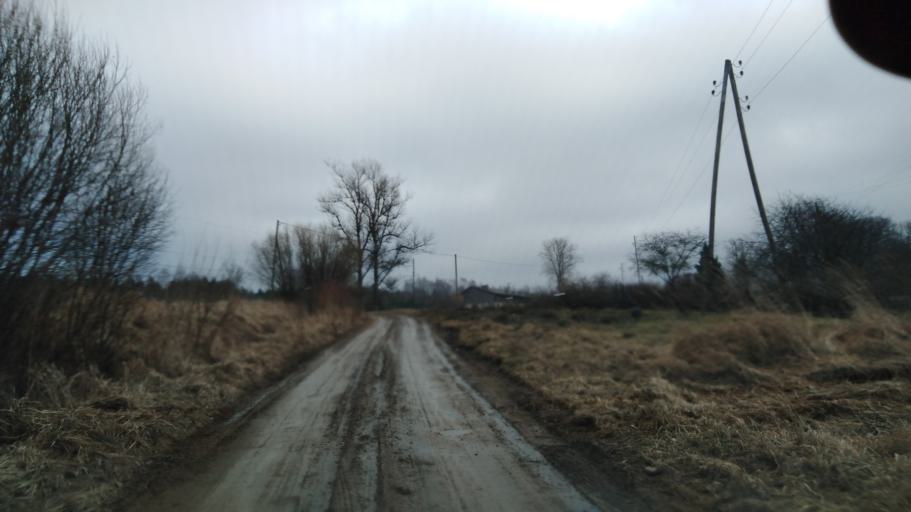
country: LV
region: Kuldigas Rajons
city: Kuldiga
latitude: 56.9838
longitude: 21.9692
